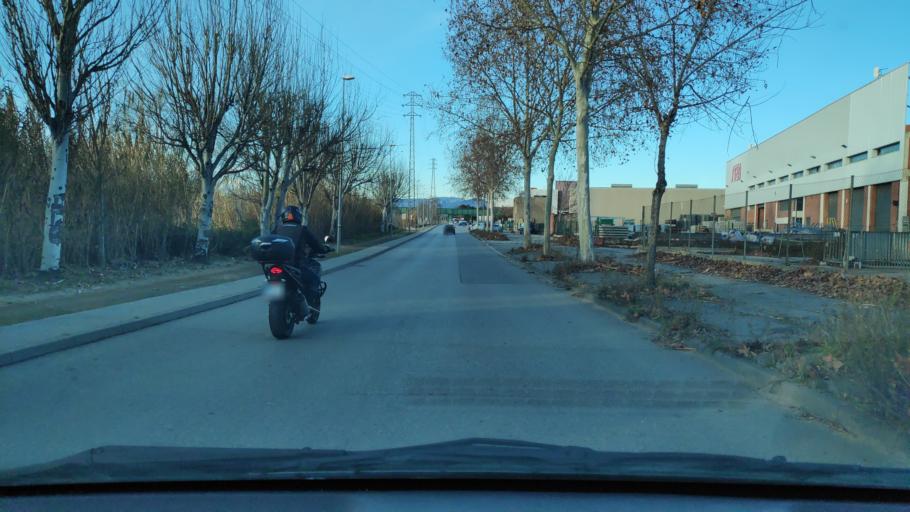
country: ES
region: Catalonia
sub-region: Provincia de Barcelona
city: Montmelo
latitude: 41.5551
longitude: 2.2347
